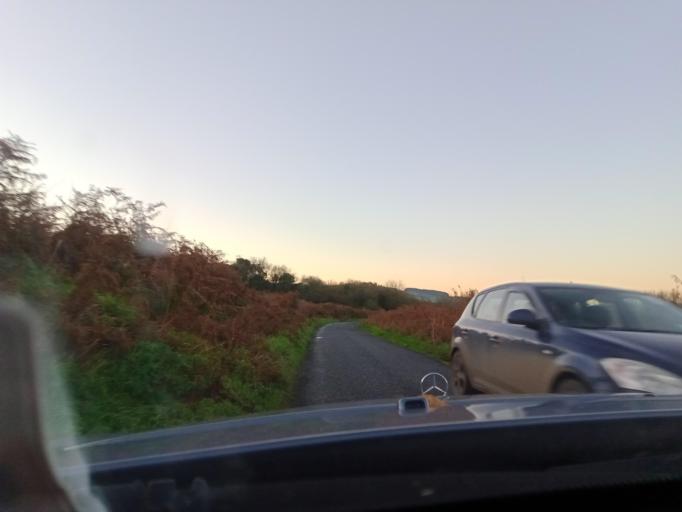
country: IE
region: Leinster
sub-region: Kilkenny
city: Thomastown
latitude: 52.4323
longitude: -7.1036
